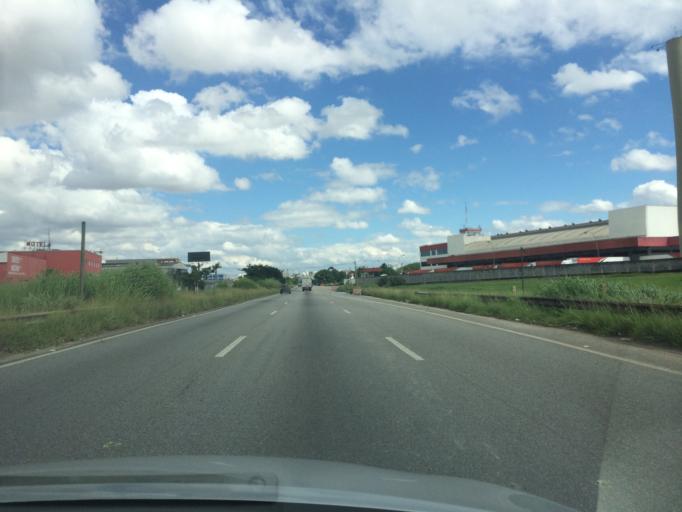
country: BR
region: Sao Paulo
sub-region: Guarulhos
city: Guarulhos
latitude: -23.5009
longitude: -46.5594
